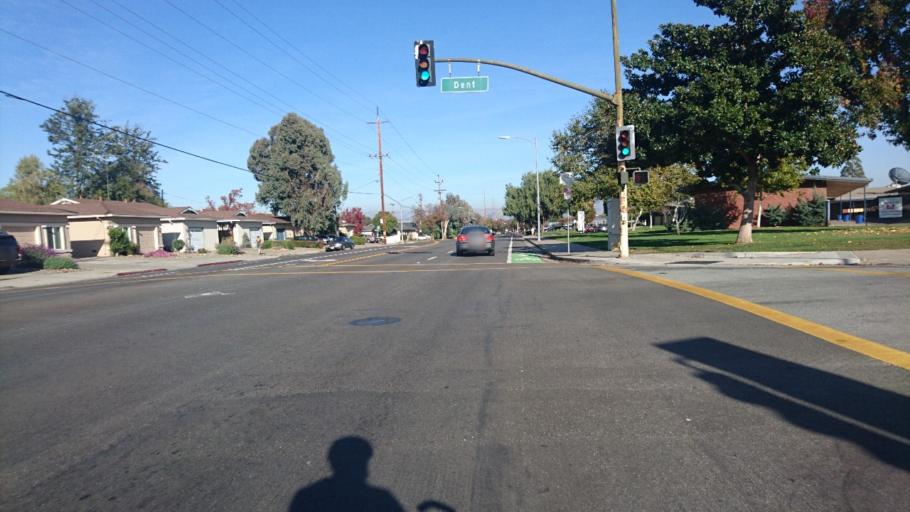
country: US
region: California
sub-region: Santa Clara County
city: Cambrian Park
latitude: 37.2537
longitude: -121.9015
